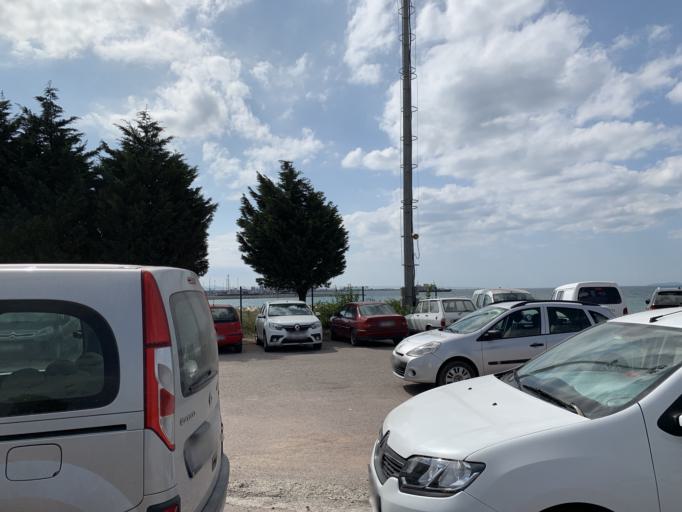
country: TR
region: Yalova
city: Taskopru
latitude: 40.6933
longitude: 29.4462
